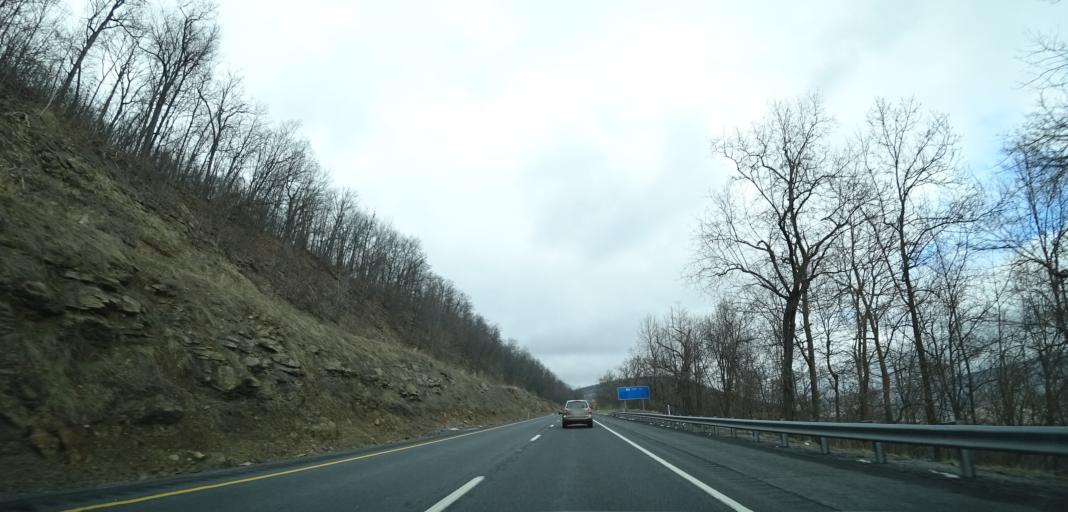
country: US
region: Pennsylvania
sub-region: Bedford County
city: Earlston
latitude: 39.8768
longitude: -78.2482
